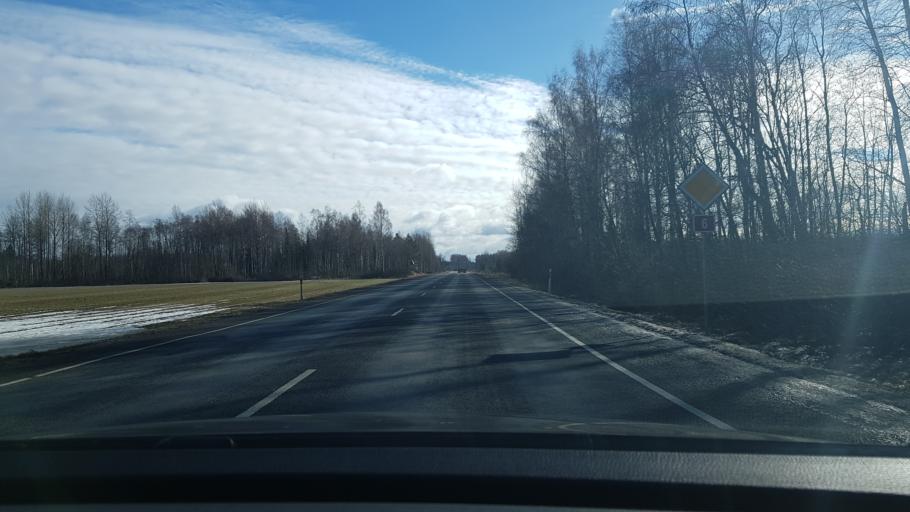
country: EE
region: Paernumaa
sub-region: Saarde vald
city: Kilingi-Nomme
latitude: 58.1804
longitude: 24.7973
